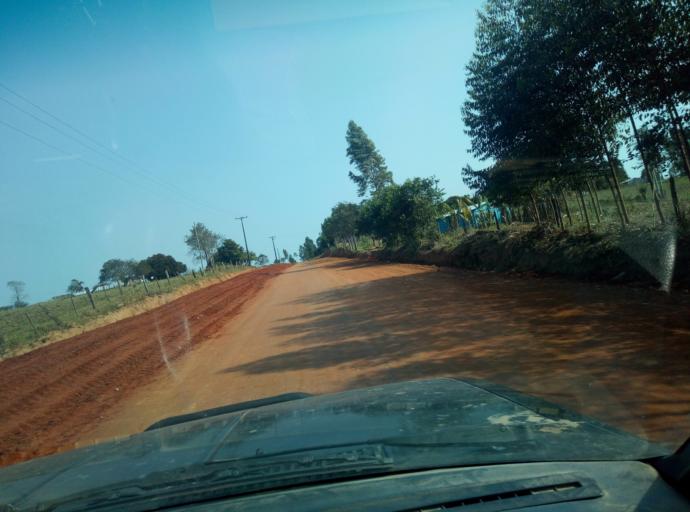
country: PY
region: Caaguazu
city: Coronel Oviedo
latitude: -25.3281
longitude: -56.3290
